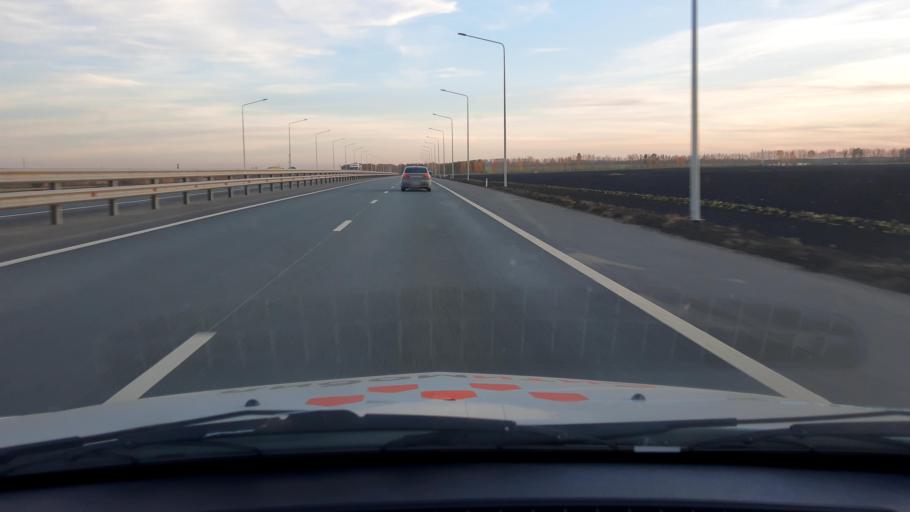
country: RU
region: Bashkortostan
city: Tolbazy
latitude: 54.2159
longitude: 55.8828
